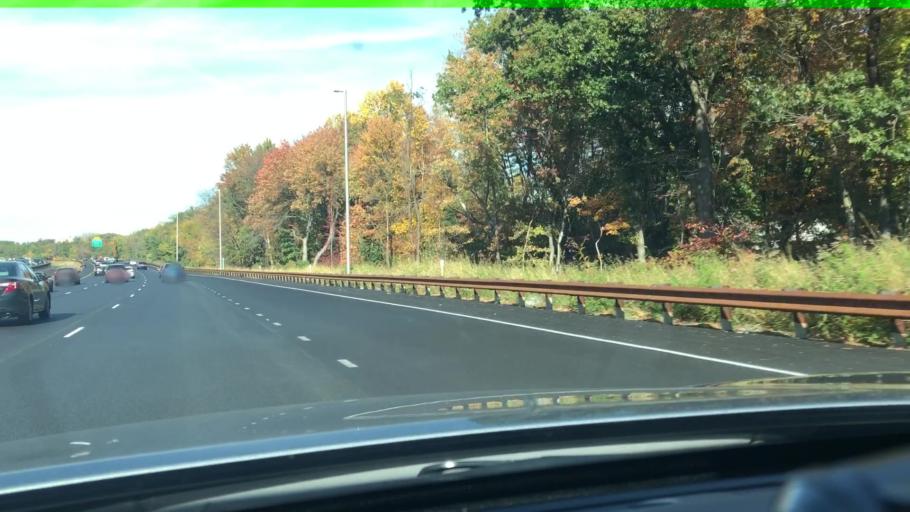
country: US
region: New Jersey
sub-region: Bergen County
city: Paramus
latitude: 40.9434
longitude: -74.0680
